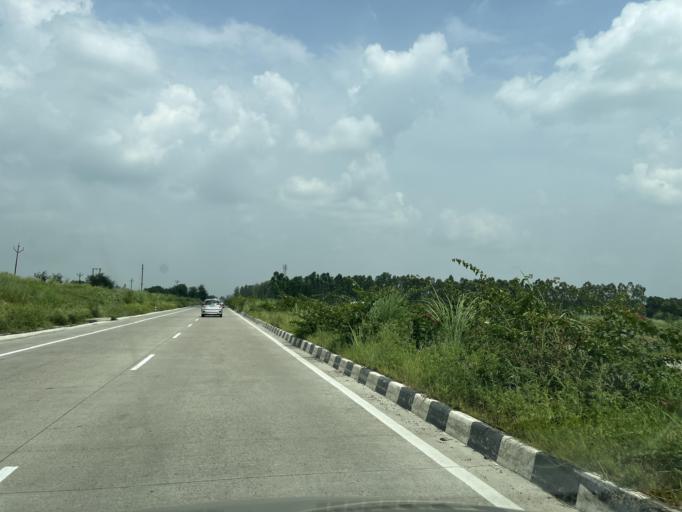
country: IN
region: Uttar Pradesh
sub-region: Bijnor
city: Sherkot
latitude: 29.3184
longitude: 78.5465
